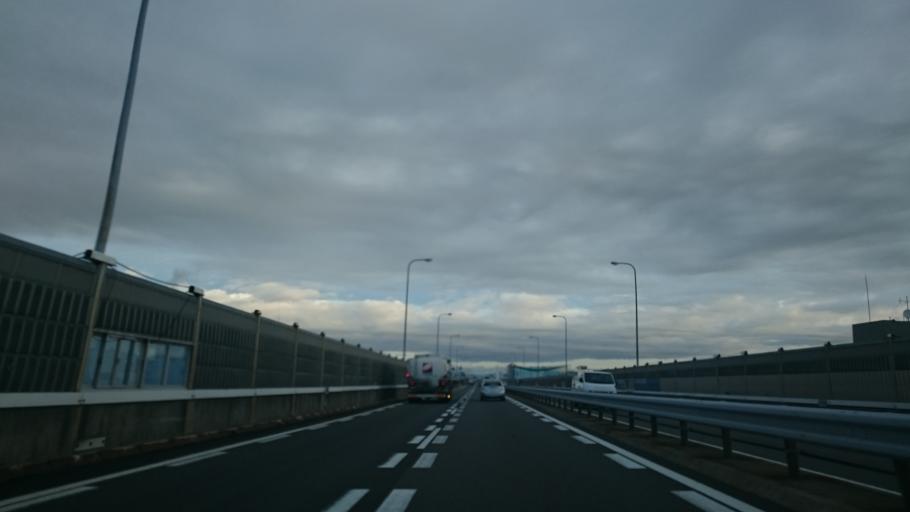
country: JP
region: Aichi
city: Kanie
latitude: 35.1838
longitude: 136.8163
